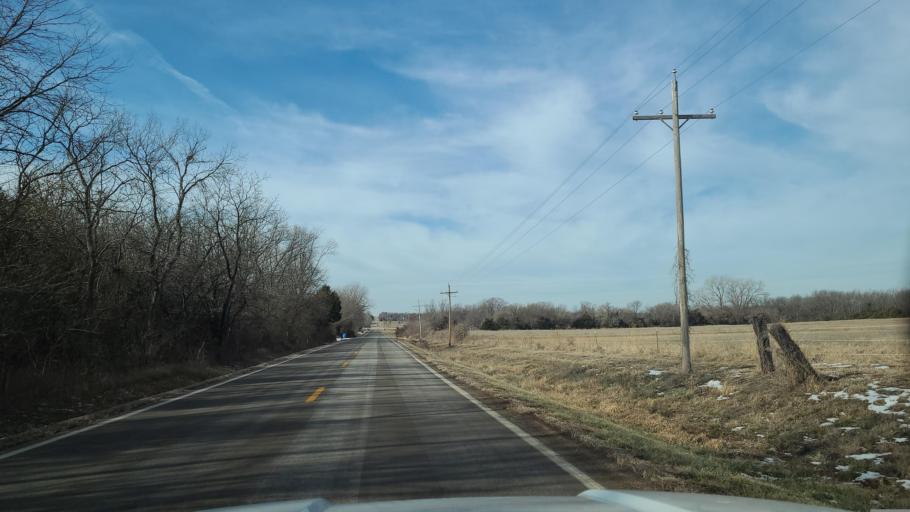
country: US
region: Kansas
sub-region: Douglas County
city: Lawrence
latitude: 38.8844
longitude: -95.1915
